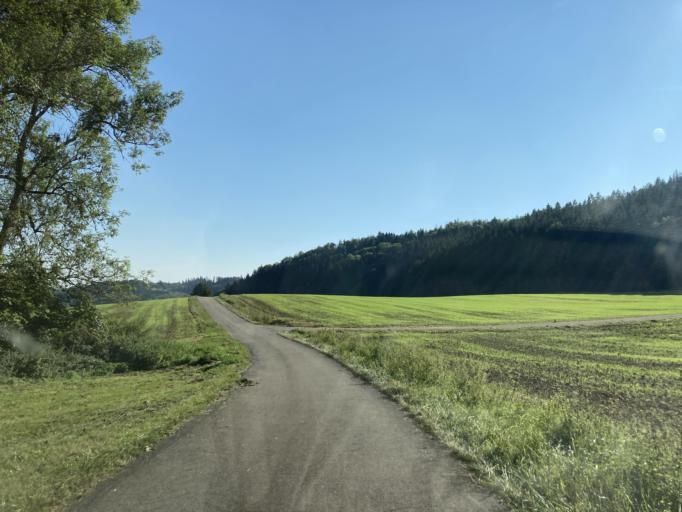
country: DE
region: Baden-Wuerttemberg
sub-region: Freiburg Region
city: Blumberg
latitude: 47.8470
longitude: 8.4998
